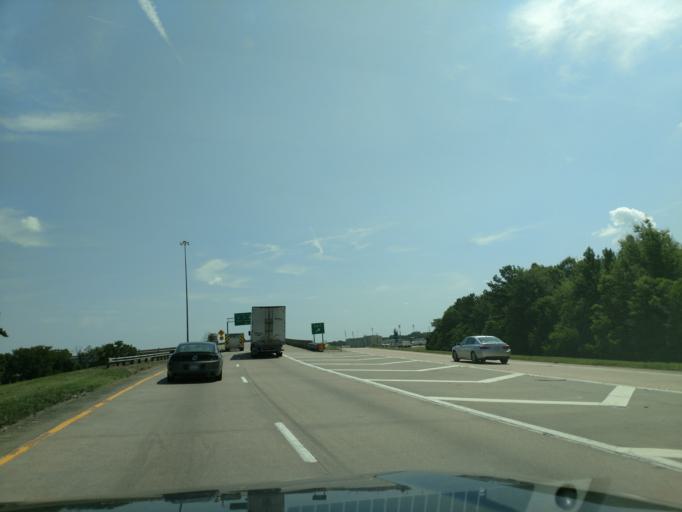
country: US
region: Mississippi
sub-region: Rankin County
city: Pearl
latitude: 32.2698
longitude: -90.1586
